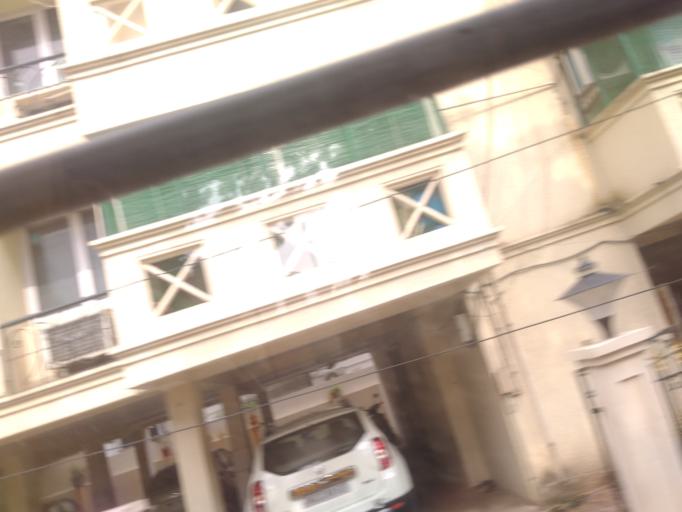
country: IN
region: Tamil Nadu
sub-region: Chennai
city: Gandhi Nagar
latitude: 13.0097
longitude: 80.2489
